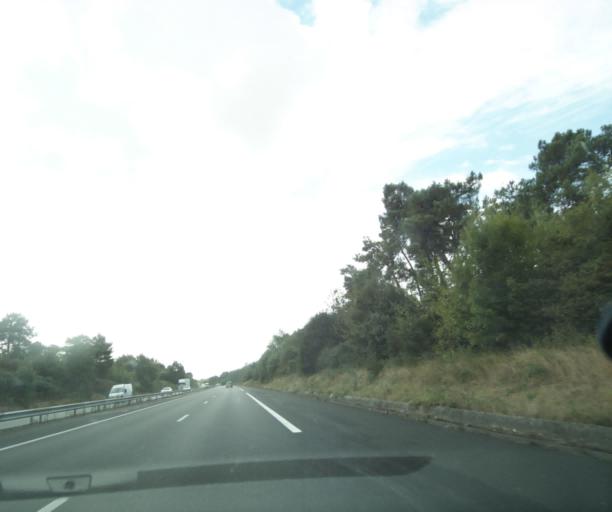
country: FR
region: Poitou-Charentes
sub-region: Departement de la Charente-Maritime
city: Thenac
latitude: 45.6543
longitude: -0.6343
